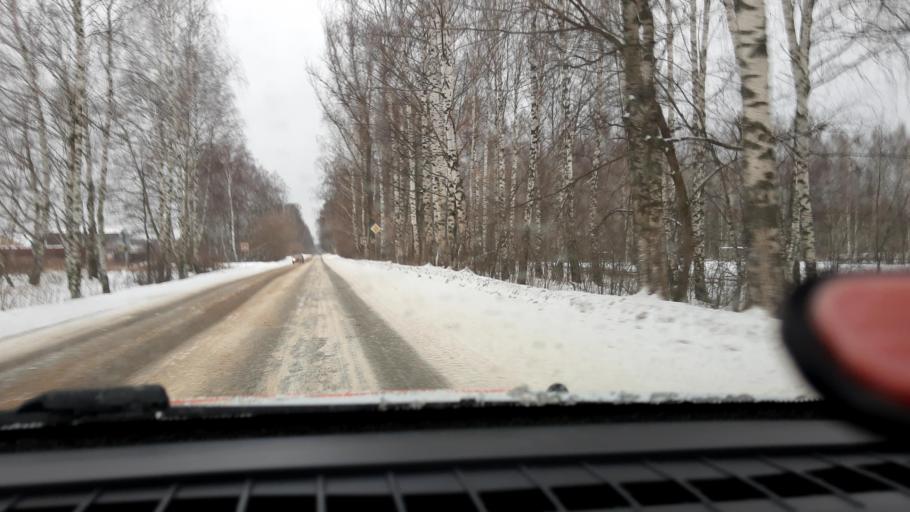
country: RU
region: Nizjnij Novgorod
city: Pamyat' Parizhskoy Kommuny
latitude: 56.2699
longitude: 44.4200
